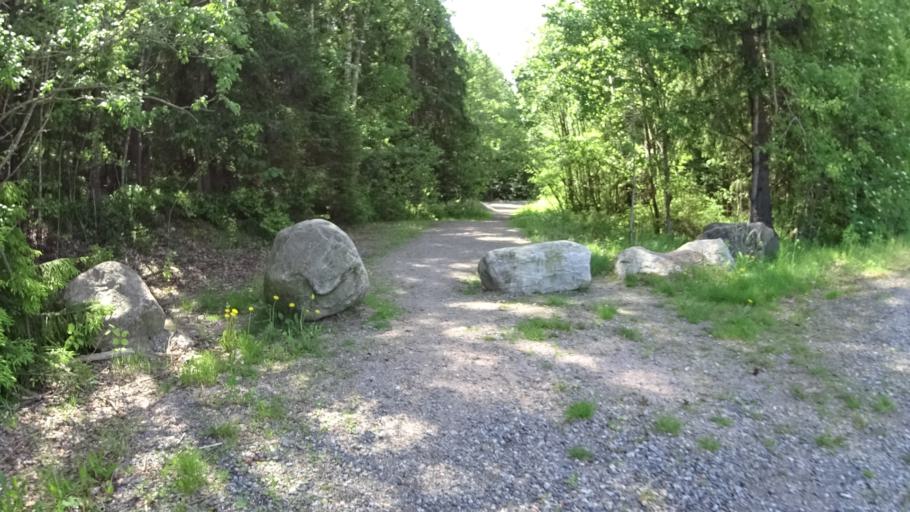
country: FI
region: Uusimaa
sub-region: Helsinki
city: Kauniainen
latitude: 60.3221
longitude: 24.7349
